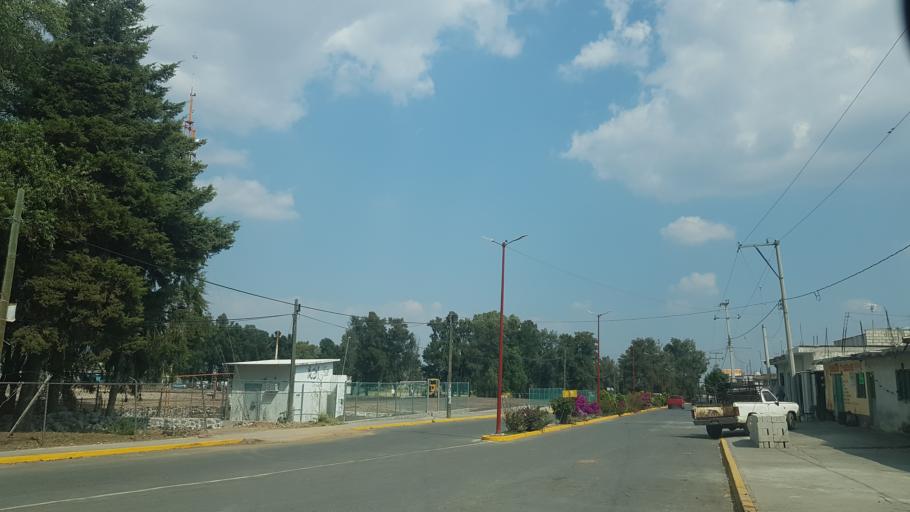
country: MX
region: Puebla
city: San Juan Amecac
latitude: 18.8313
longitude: -98.6596
